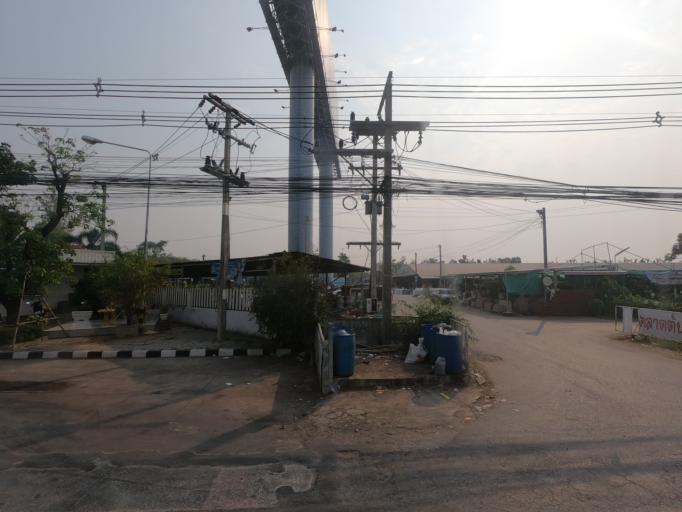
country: TH
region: Khon Kaen
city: Khon Kaen
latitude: 16.3818
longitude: 102.8105
